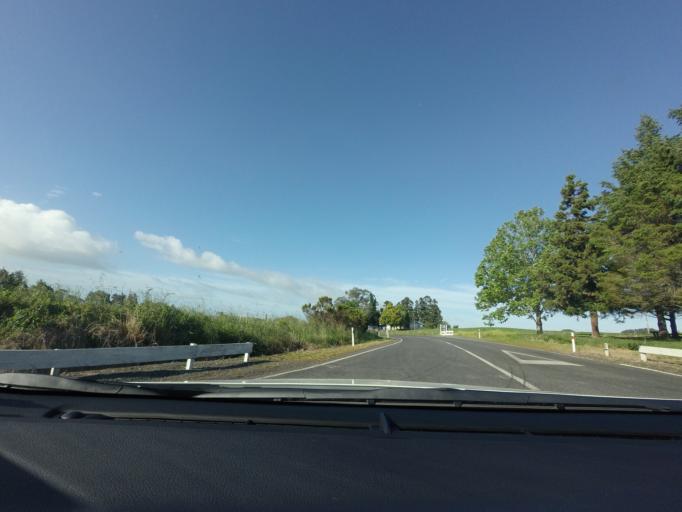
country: NZ
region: Waikato
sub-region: Hauraki District
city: Paeroa
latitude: -37.4728
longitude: 175.5099
